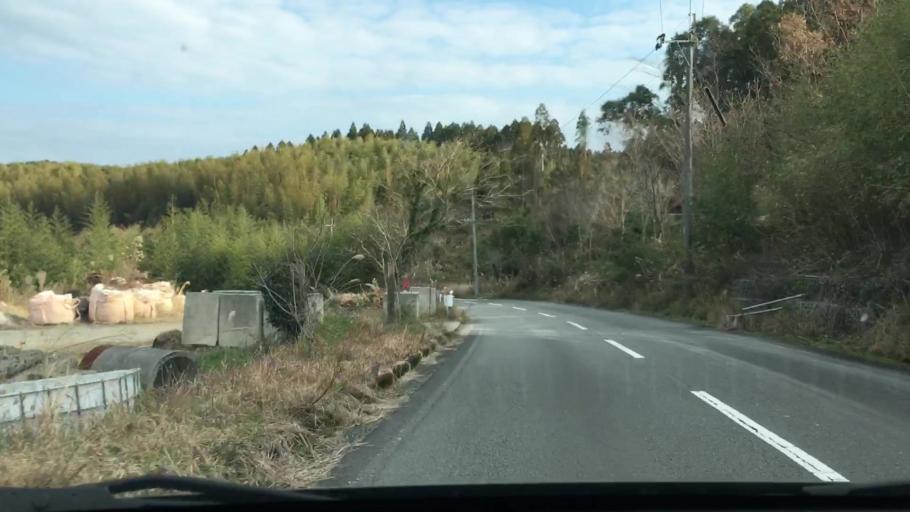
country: JP
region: Miyazaki
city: Nichinan
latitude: 31.6091
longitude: 131.3333
